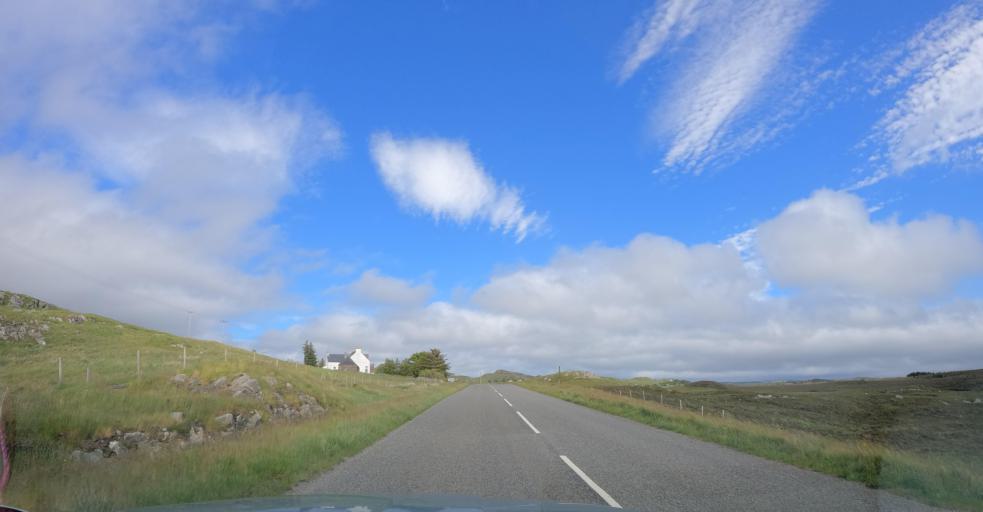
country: GB
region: Scotland
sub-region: Eilean Siar
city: Stornoway
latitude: 58.1040
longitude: -6.5554
